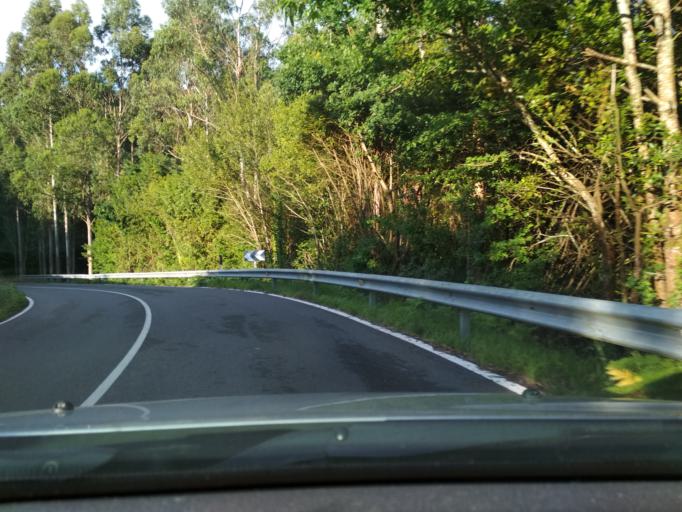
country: ES
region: Galicia
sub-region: Provincia da Coruna
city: Outes
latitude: 42.8914
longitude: -8.9310
